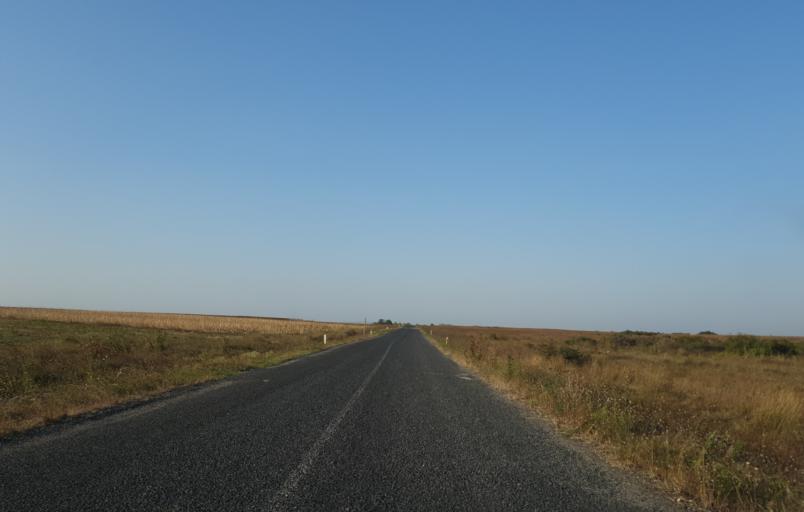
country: TR
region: Tekirdag
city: Beyazkoy
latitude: 41.4029
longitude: 27.7586
